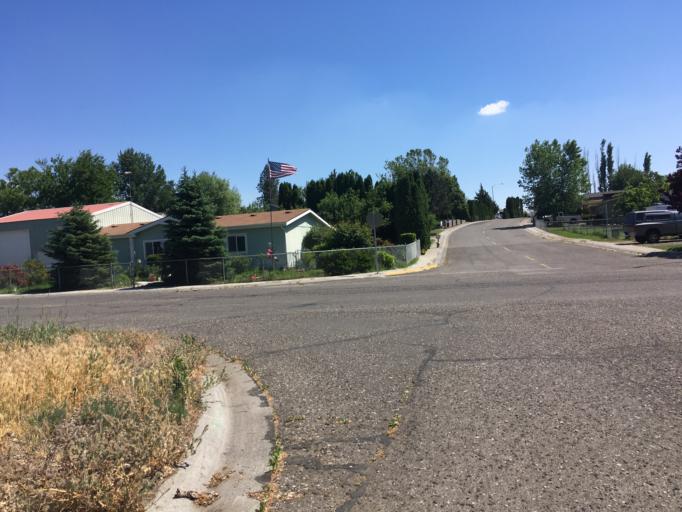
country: US
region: Oregon
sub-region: Morrow County
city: Boardman
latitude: 45.8316
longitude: -119.7098
